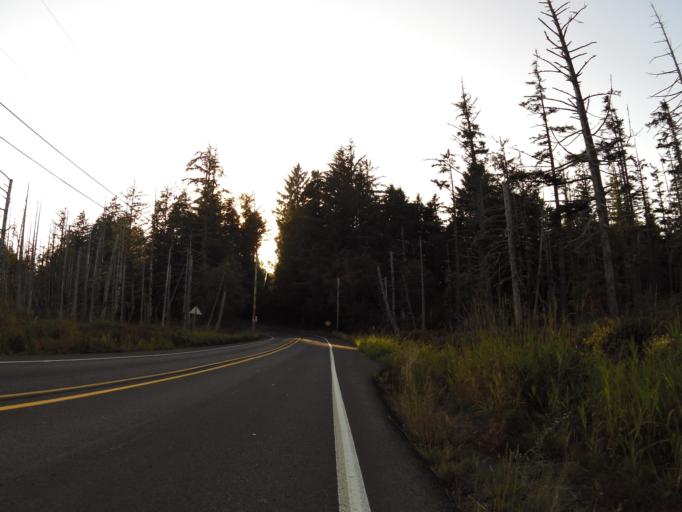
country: US
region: Oregon
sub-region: Lincoln County
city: Lincoln City
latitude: 44.9616
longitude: -124.0040
